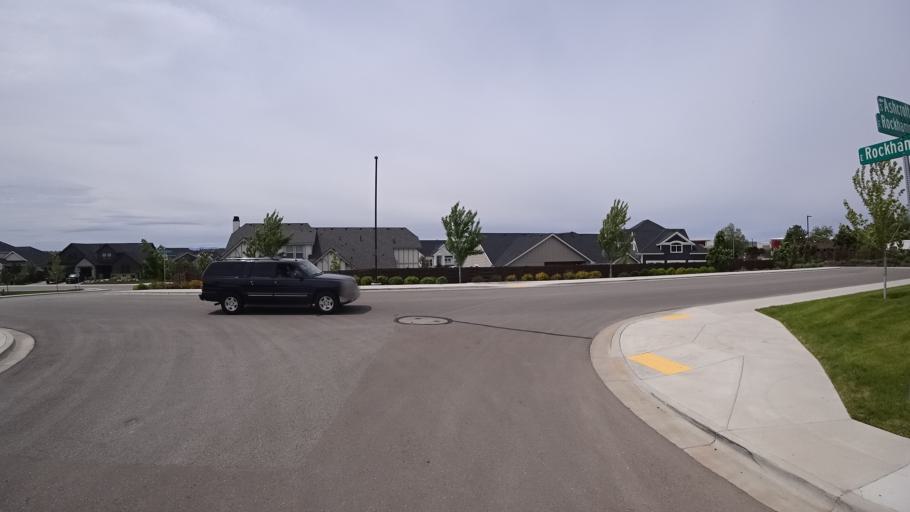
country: US
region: Idaho
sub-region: Ada County
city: Meridian
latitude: 43.5570
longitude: -116.3427
